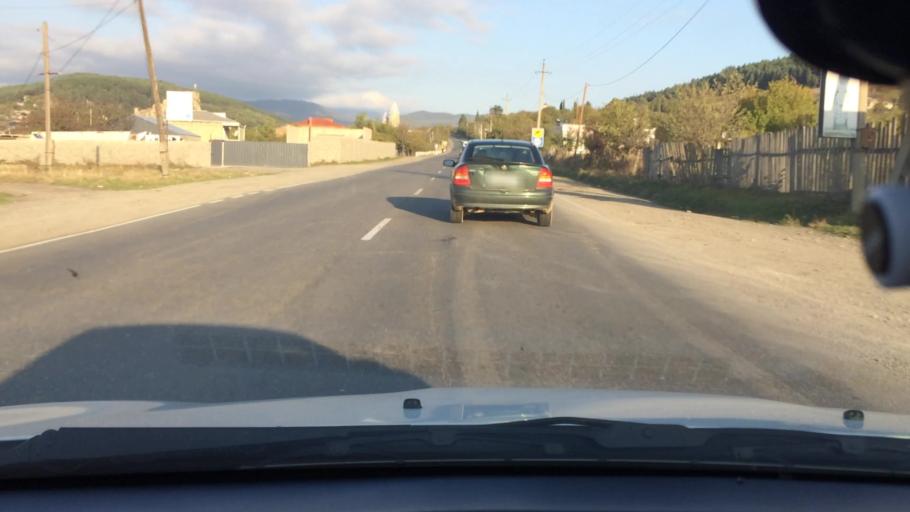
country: GE
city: Surami
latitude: 42.0145
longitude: 43.5736
